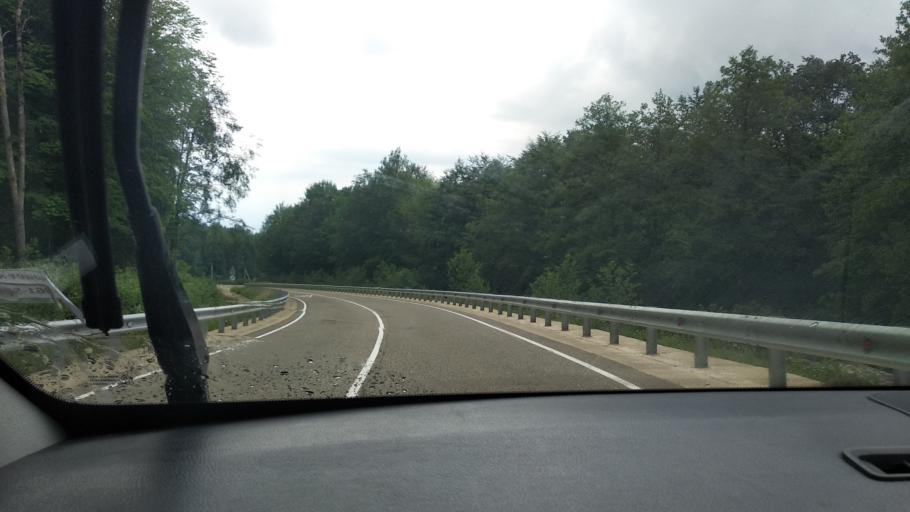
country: RU
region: Adygeya
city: Kamennomostskiy
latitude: 44.2495
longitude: 39.9764
